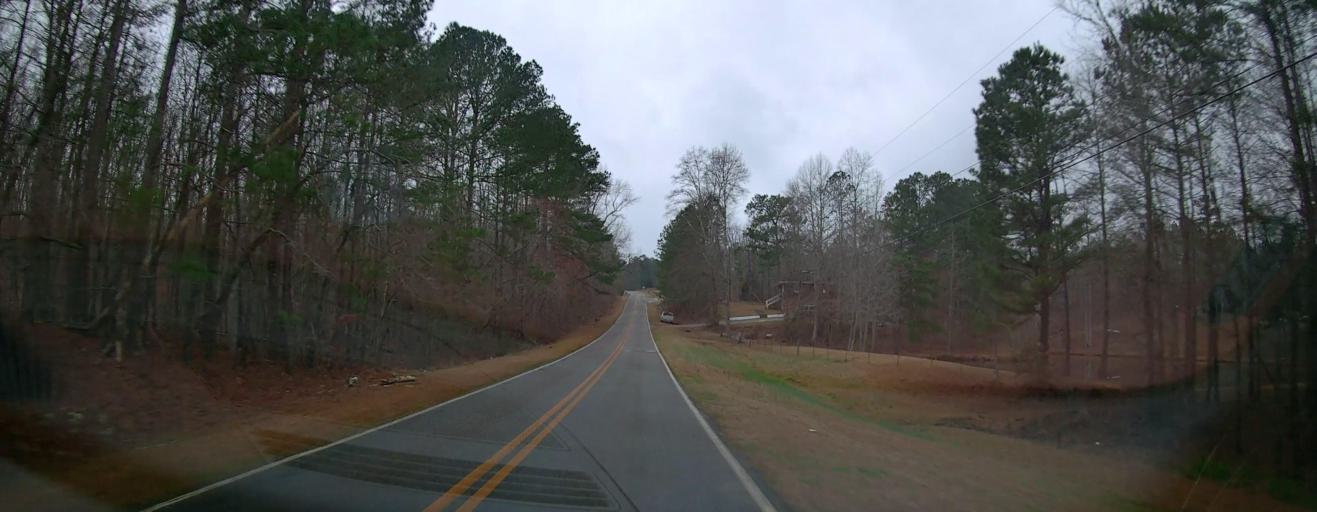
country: US
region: Georgia
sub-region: Lamar County
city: Barnesville
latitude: 33.0678
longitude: -84.1199
